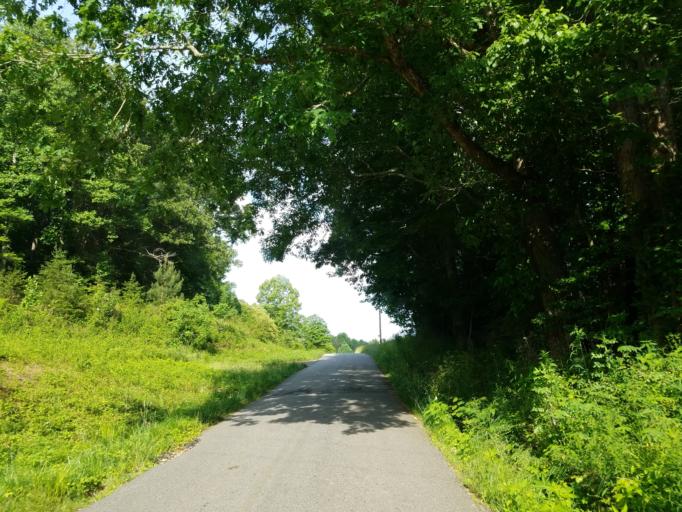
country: US
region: Georgia
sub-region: Lumpkin County
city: Dahlonega
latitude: 34.5600
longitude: -84.0741
